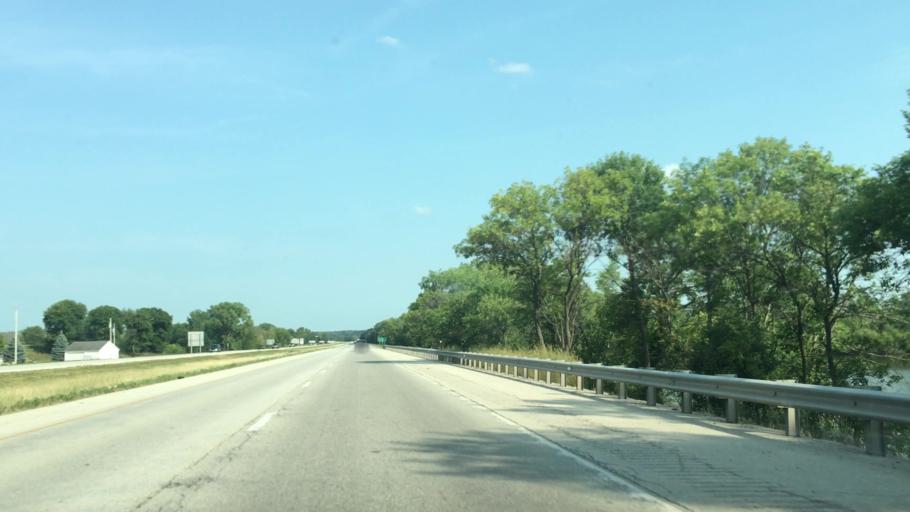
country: US
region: Illinois
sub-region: Rock Island County
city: Milan
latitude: 41.4562
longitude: -90.6036
